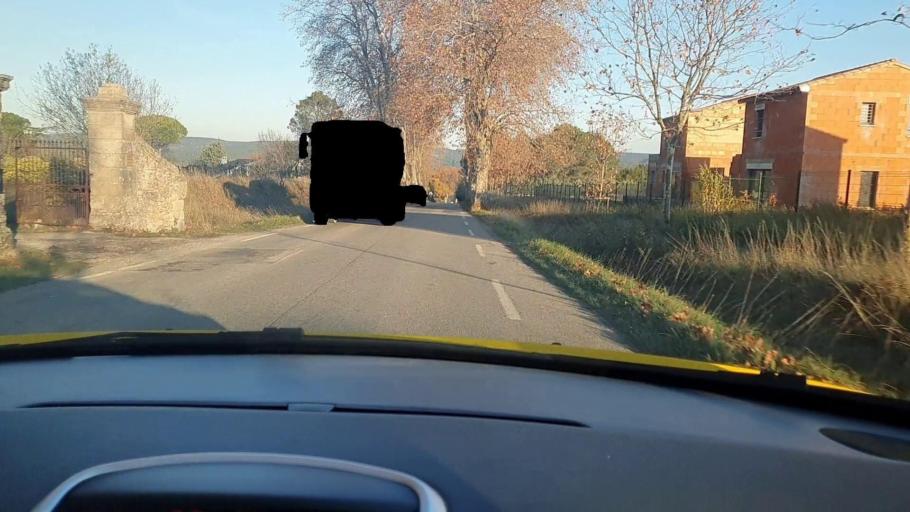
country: FR
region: Languedoc-Roussillon
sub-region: Departement du Gard
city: Uzes
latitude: 44.0270
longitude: 4.4126
